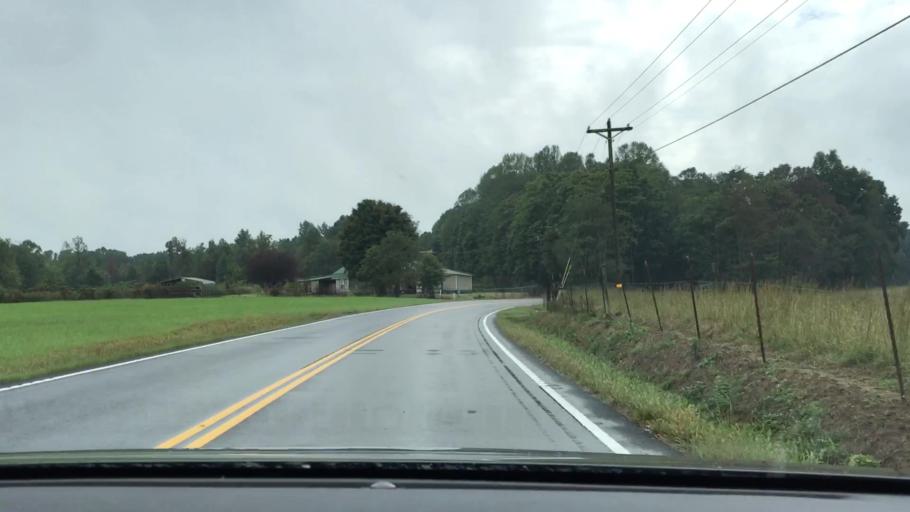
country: US
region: Tennessee
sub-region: Macon County
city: Red Boiling Springs
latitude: 36.4645
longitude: -85.8792
